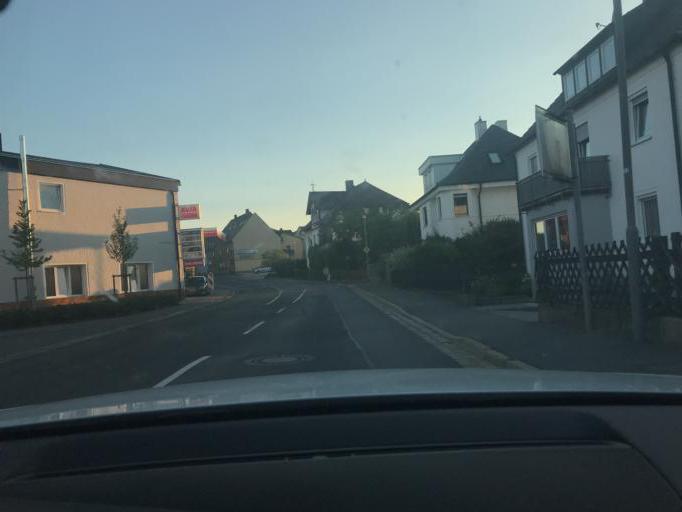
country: DE
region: Bavaria
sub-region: Upper Palatinate
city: Auerbach
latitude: 49.6951
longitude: 11.6299
